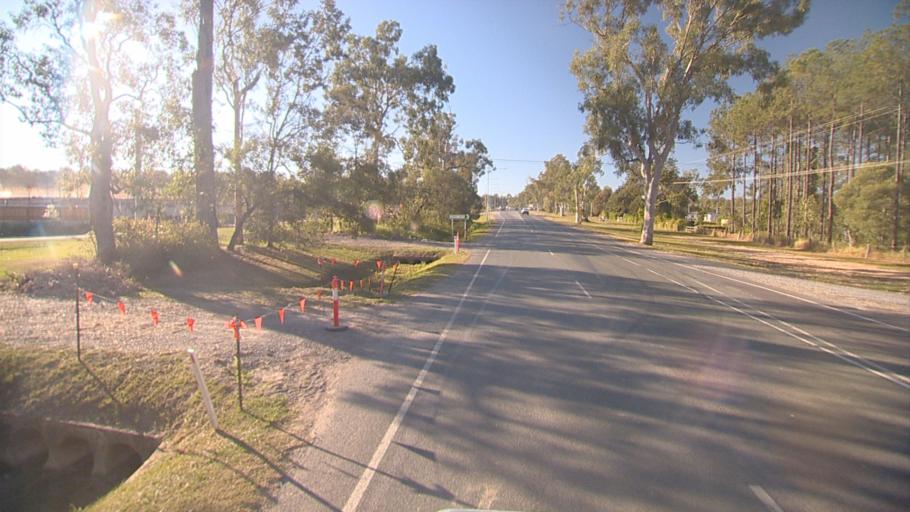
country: AU
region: Queensland
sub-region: Logan
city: Logan Reserve
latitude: -27.7132
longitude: 153.0930
